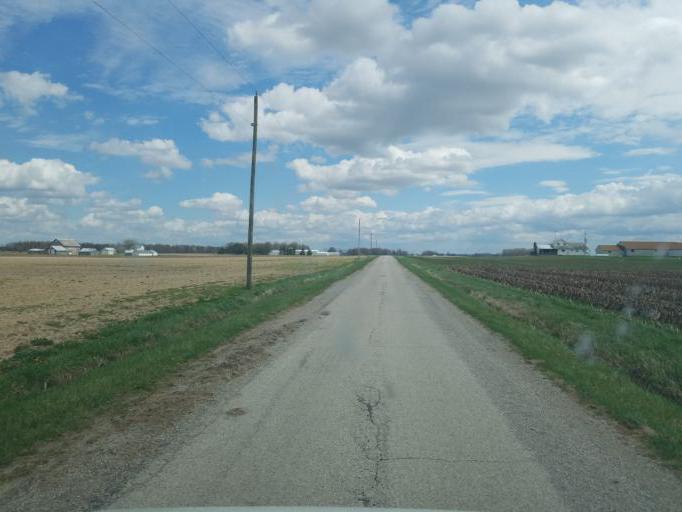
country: US
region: Ohio
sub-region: Crawford County
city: Bucyrus
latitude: 40.9216
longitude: -82.9076
